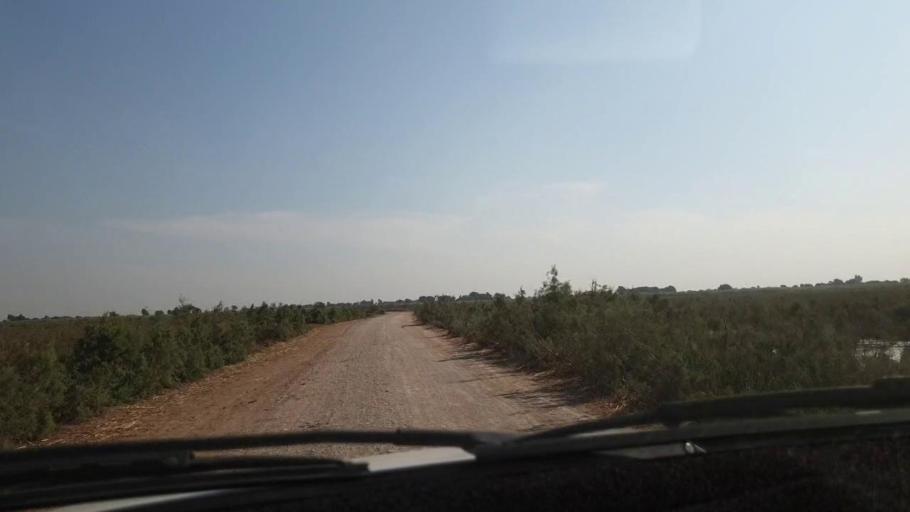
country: PK
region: Sindh
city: Bulri
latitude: 24.9525
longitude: 68.4217
